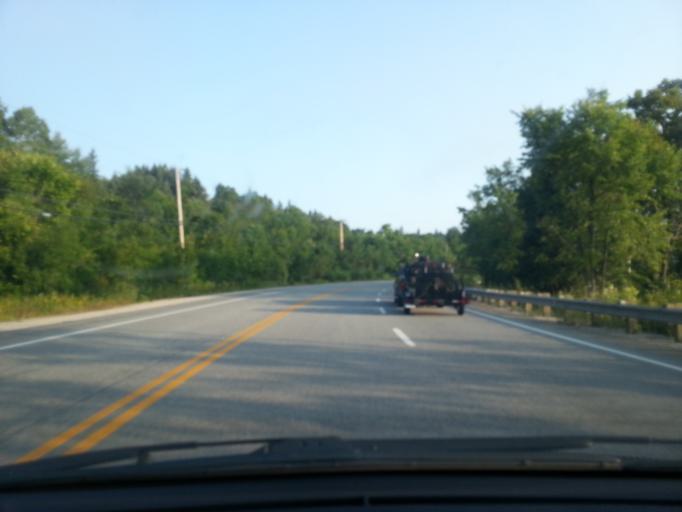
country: CA
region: Quebec
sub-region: Outaouais
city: Wakefield
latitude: 45.6640
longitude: -75.9274
